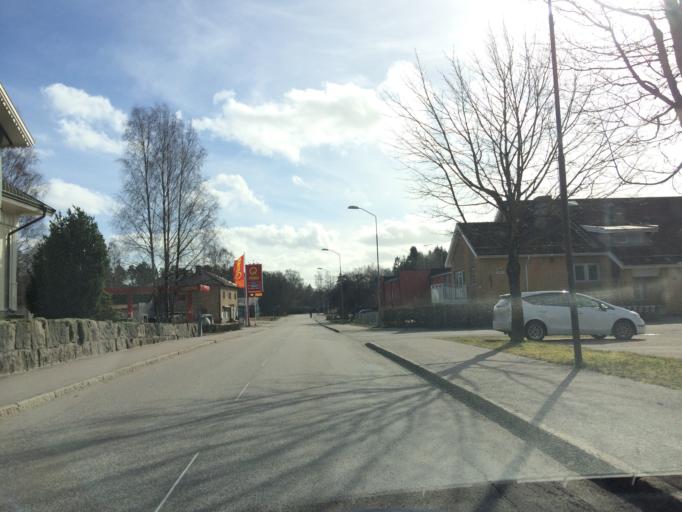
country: SE
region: Halland
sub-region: Hylte Kommun
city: Hyltebruk
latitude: 56.8283
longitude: 13.4389
